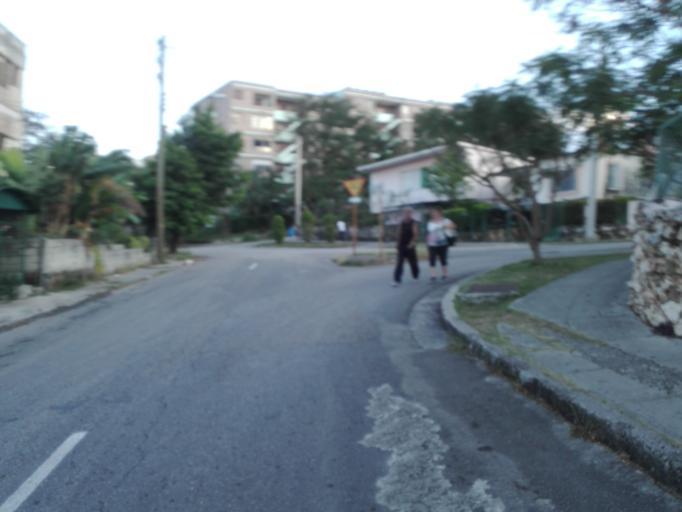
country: CU
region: La Habana
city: Cerro
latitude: 23.1160
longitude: -82.3977
